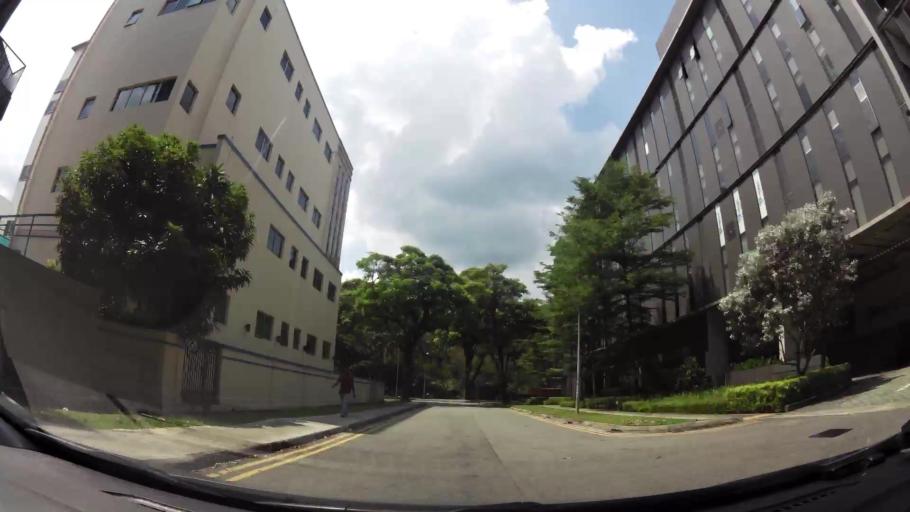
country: SG
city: Singapore
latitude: 1.3835
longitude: 103.8265
